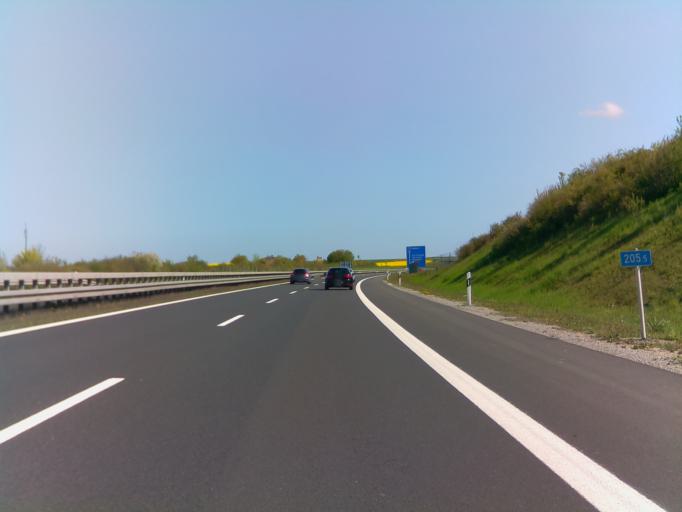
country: DE
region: Bavaria
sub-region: Regierungsbezirk Unterfranken
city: Oerlenbach
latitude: 50.1322
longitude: 10.1497
